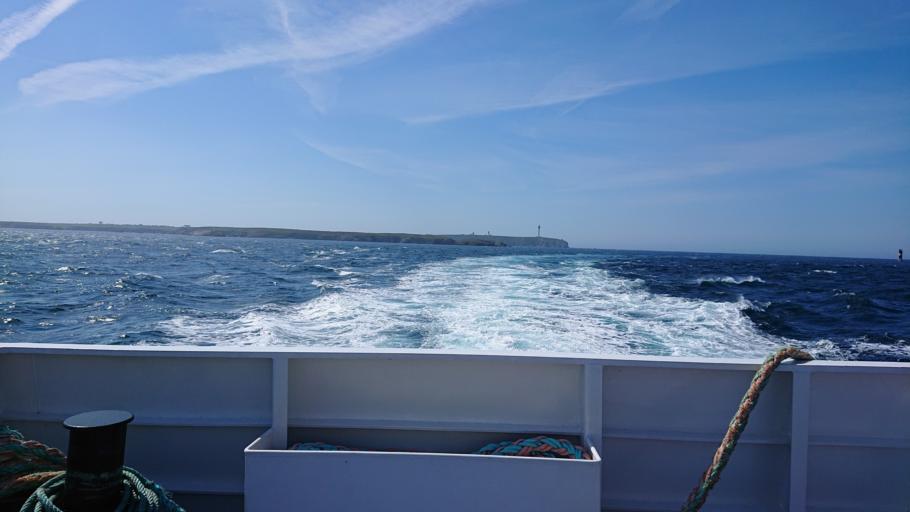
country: FR
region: Brittany
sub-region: Departement du Finistere
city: Porspoder
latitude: 48.4552
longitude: -5.0152
